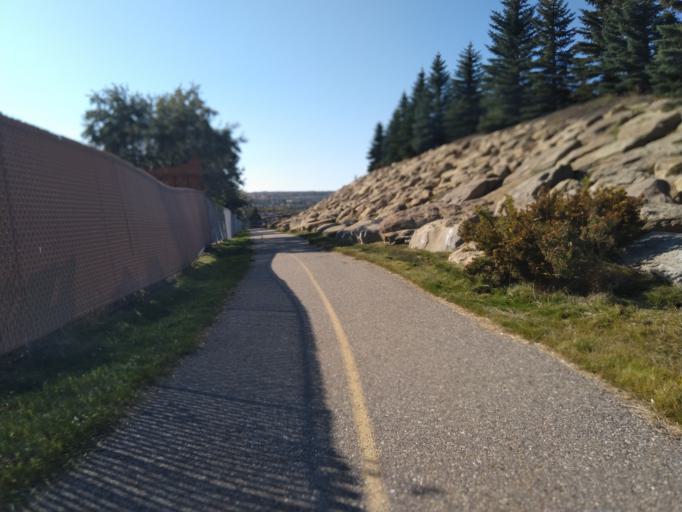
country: CA
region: Alberta
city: Calgary
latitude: 51.1477
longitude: -114.0848
